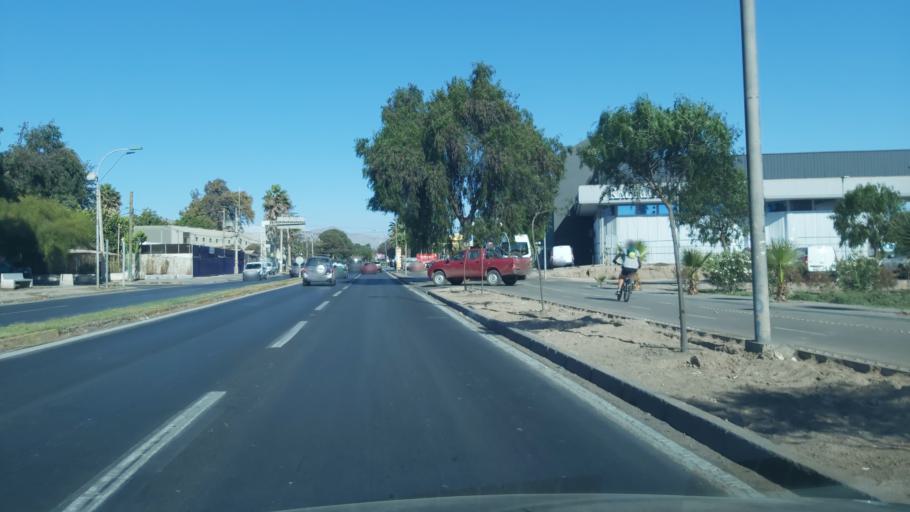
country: CL
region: Atacama
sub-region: Provincia de Copiapo
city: Copiapo
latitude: -27.3710
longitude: -70.3344
